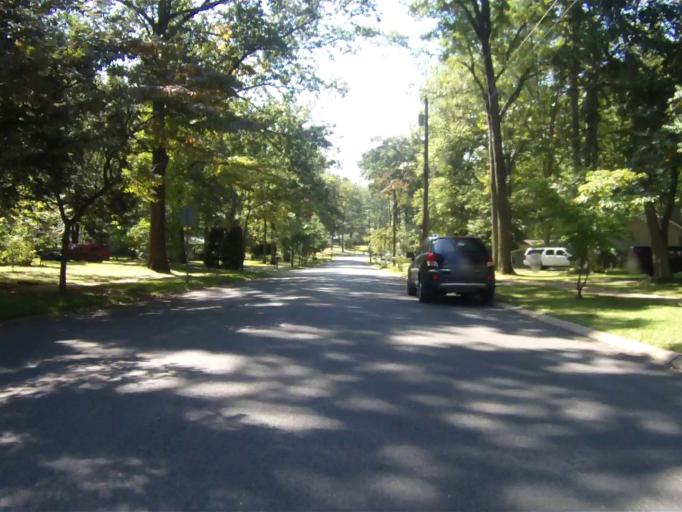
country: US
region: Pennsylvania
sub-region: Centre County
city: Park Forest Village
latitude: 40.8067
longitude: -77.9122
